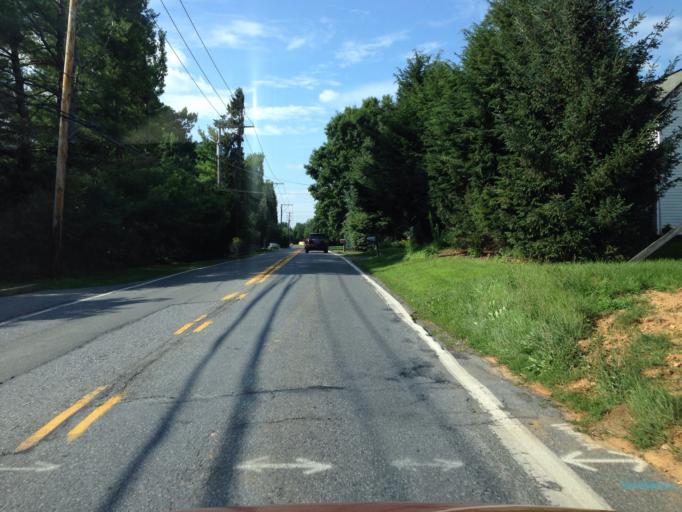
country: US
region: Pennsylvania
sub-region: Lancaster County
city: East Petersburg
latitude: 40.0968
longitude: -76.3288
